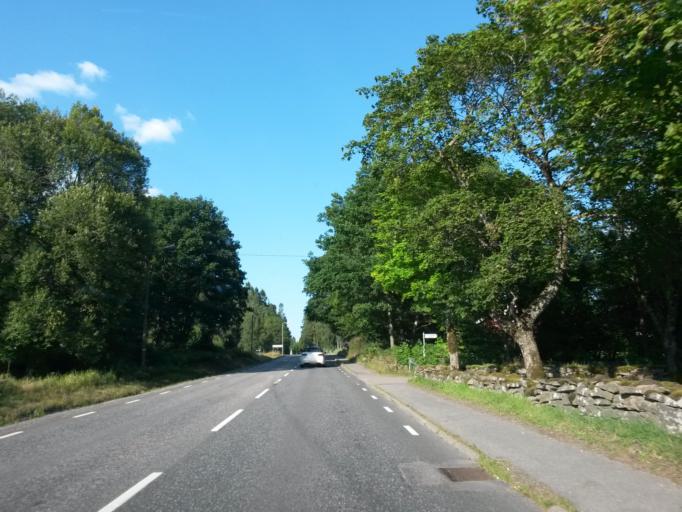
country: SE
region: Vaestra Goetaland
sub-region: Lerums Kommun
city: Grabo
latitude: 57.9284
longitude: 12.3633
